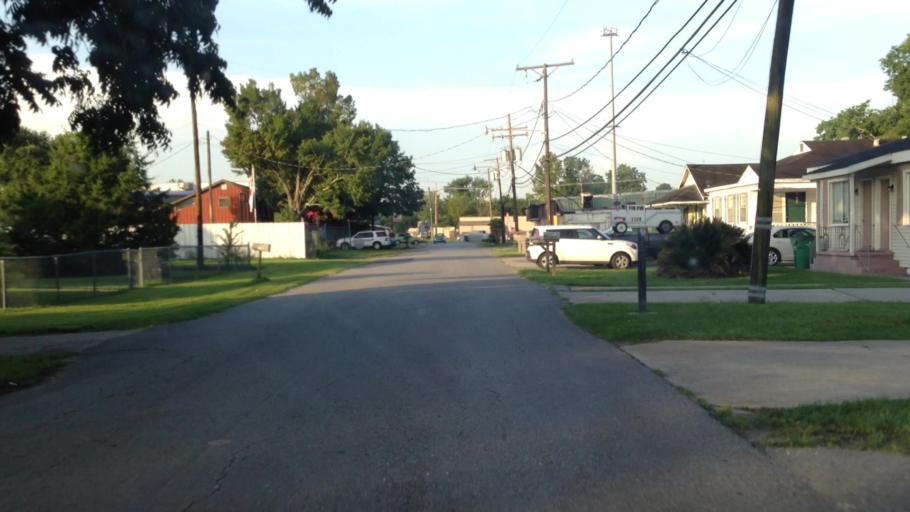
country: US
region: Louisiana
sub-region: Jefferson Parish
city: Bridge City
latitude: 29.9311
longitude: -90.1596
